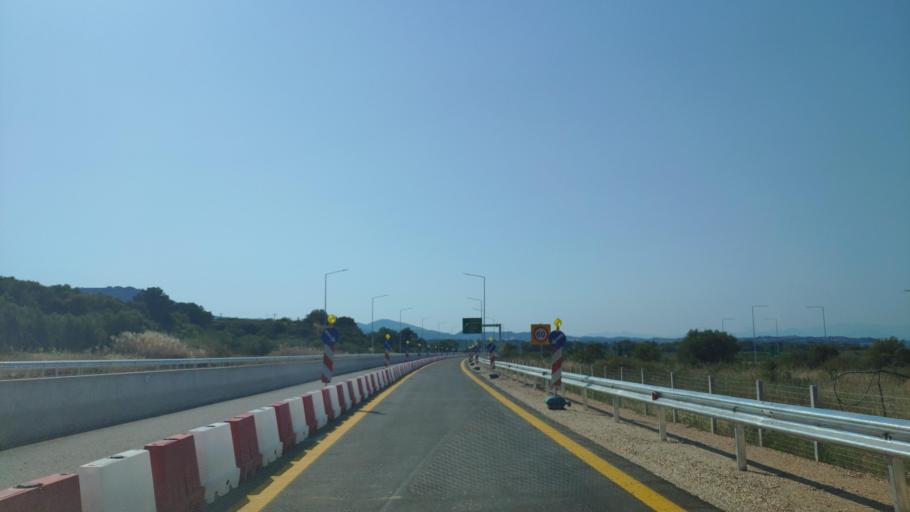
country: GR
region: West Greece
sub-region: Nomos Aitolias kai Akarnanias
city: Katouna
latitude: 38.8671
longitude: 21.0660
